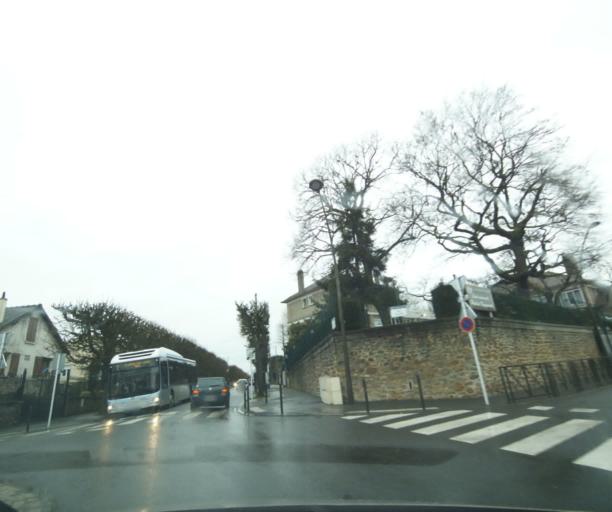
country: FR
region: Ile-de-France
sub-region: Departement du Val-de-Marne
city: Ablon-sur-Seine
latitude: 48.7355
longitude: 2.4165
